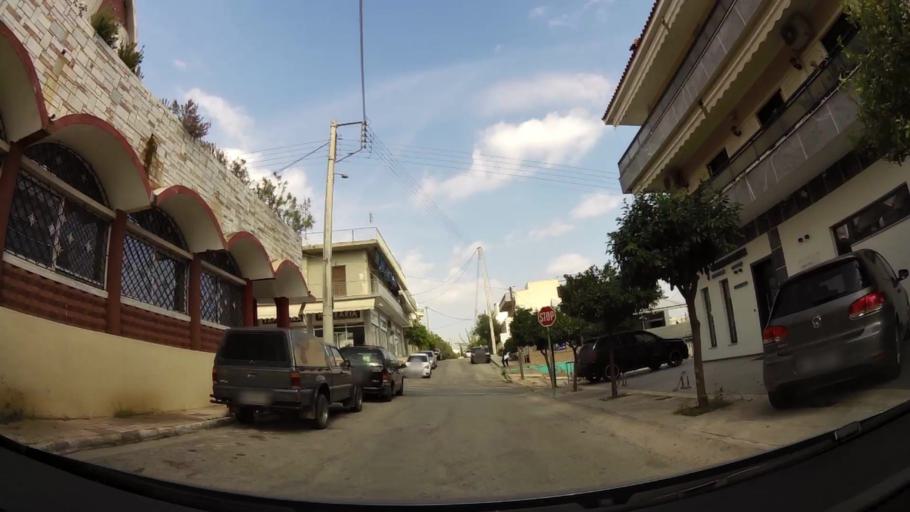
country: GR
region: Attica
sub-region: Nomarchia Athinas
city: Kamateron
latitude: 38.0486
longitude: 23.6970
